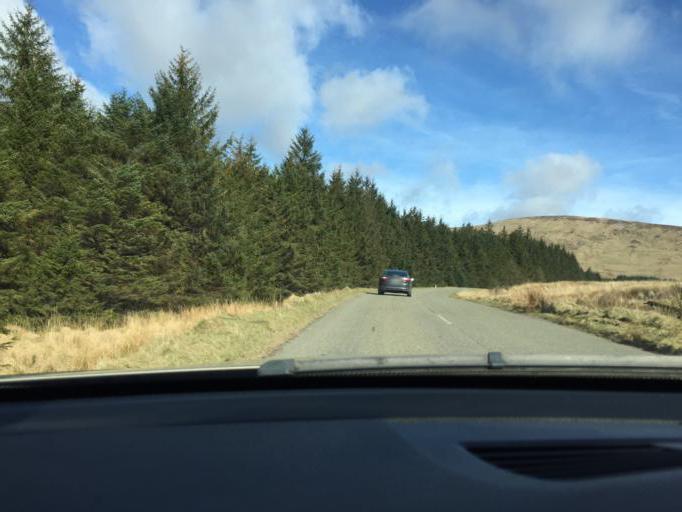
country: IE
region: Leinster
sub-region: Wicklow
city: Valleymount
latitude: 53.0574
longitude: -6.4188
